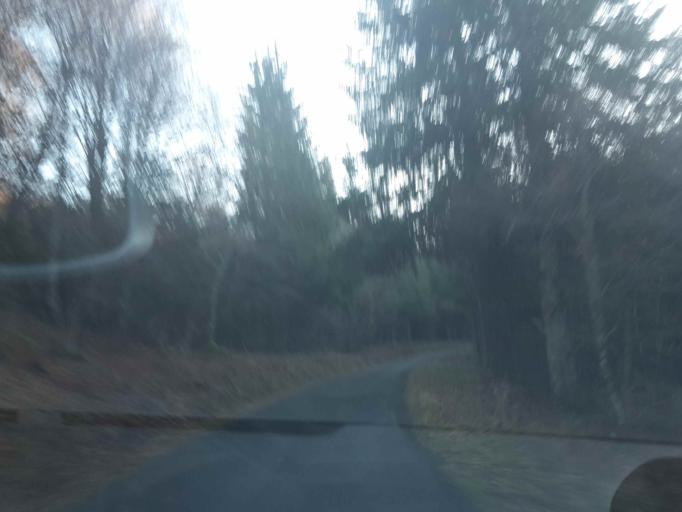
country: FR
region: Auvergne
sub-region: Departement du Cantal
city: Riom-es-Montagnes
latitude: 45.2167
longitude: 2.5794
